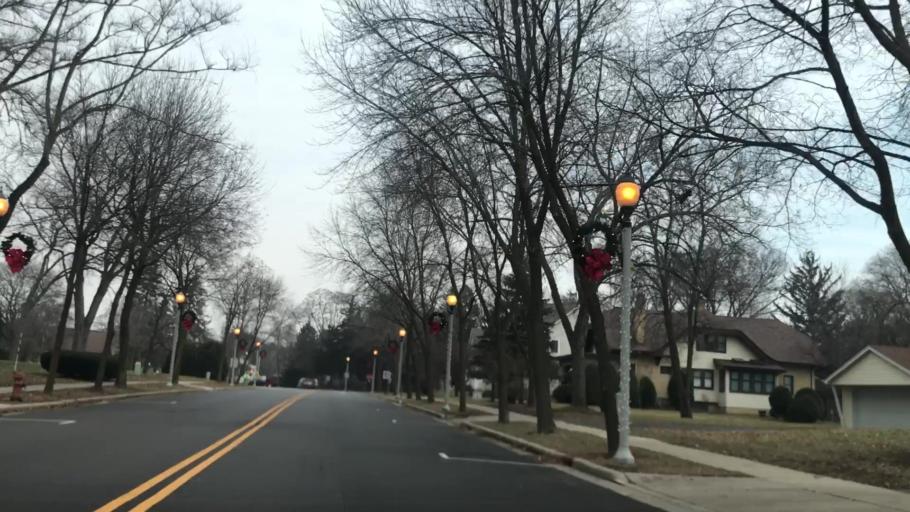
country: US
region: Wisconsin
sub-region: Ozaukee County
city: Thiensville
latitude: 43.2352
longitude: -87.9812
